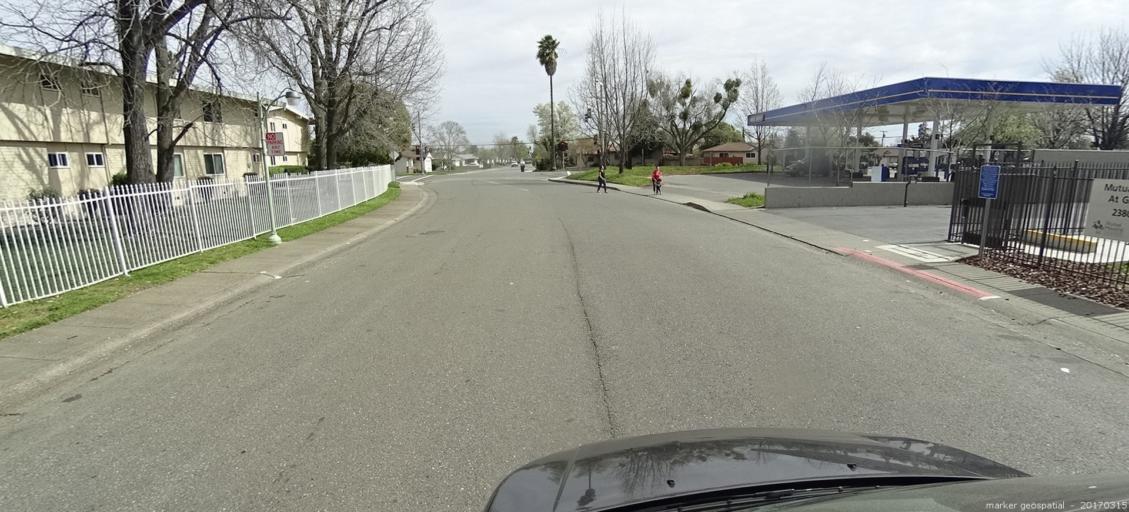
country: US
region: California
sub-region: Sacramento County
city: Parkway
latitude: 38.5166
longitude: -121.4841
